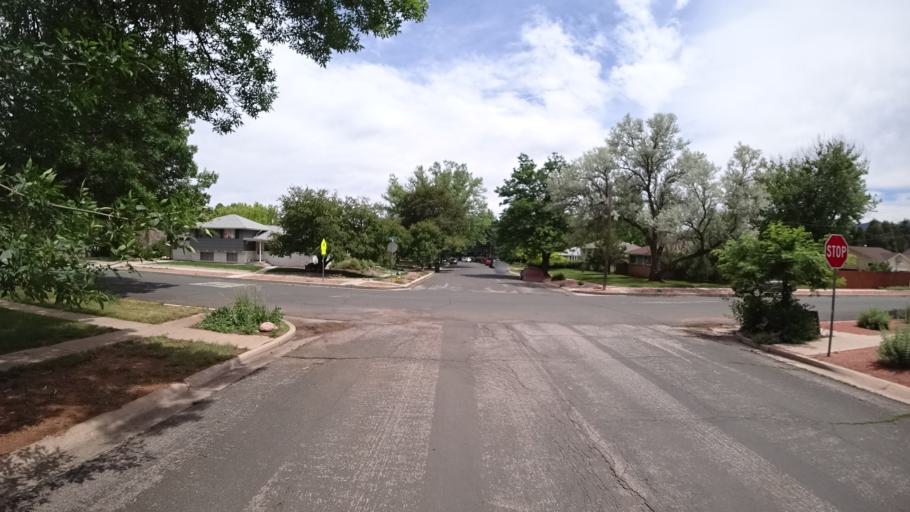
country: US
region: Colorado
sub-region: El Paso County
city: Manitou Springs
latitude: 38.8657
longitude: -104.8703
